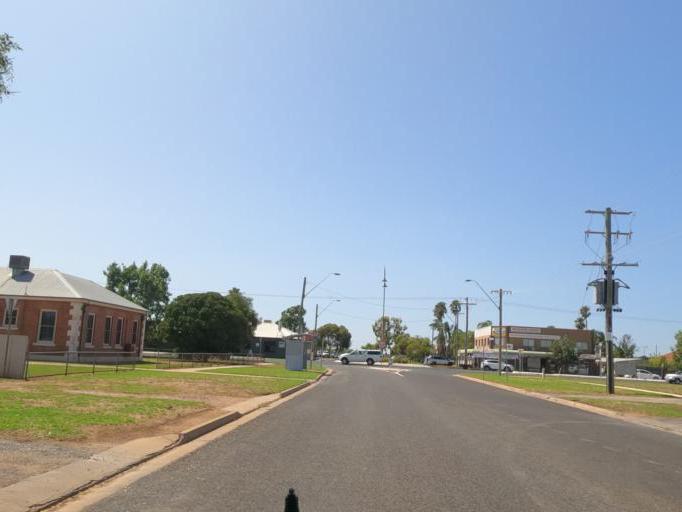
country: AU
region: New South Wales
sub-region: Corowa Shire
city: Mulwala
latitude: -35.9890
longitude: 146.0045
